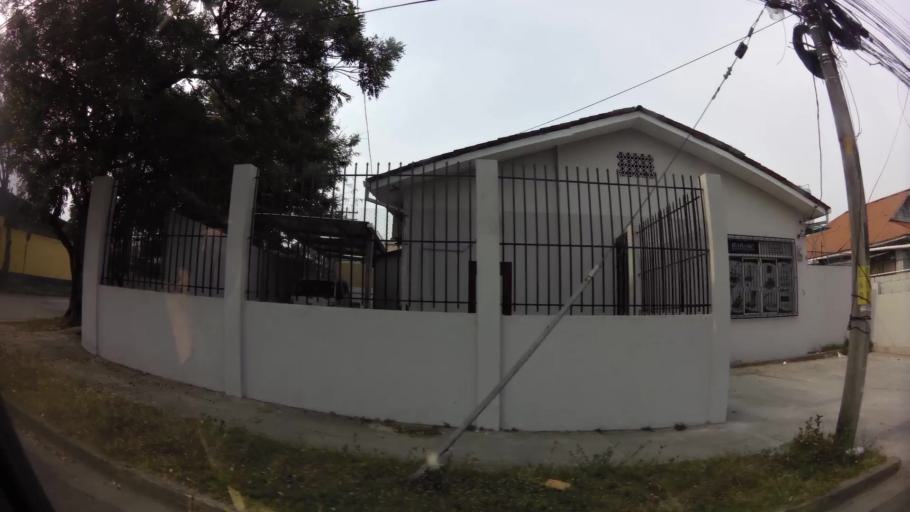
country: HN
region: Cortes
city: San Pedro Sula
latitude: 15.5018
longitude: -88.0335
